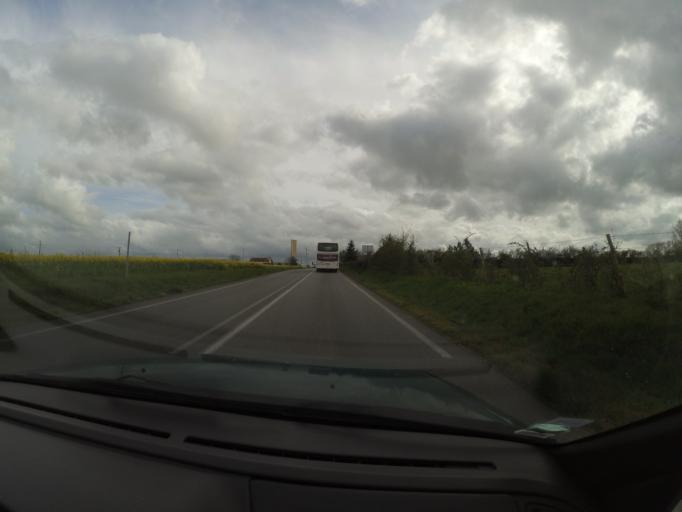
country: FR
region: Pays de la Loire
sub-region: Departement de Maine-et-Loire
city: Lire
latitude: 47.3279
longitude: -1.1670
